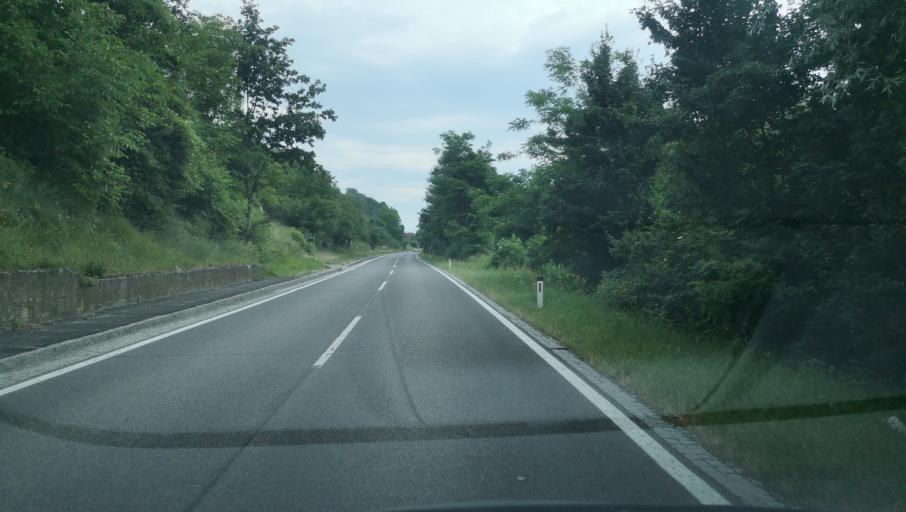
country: AT
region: Lower Austria
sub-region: Politischer Bezirk Melk
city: Leiben
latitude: 48.2274
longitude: 15.2767
